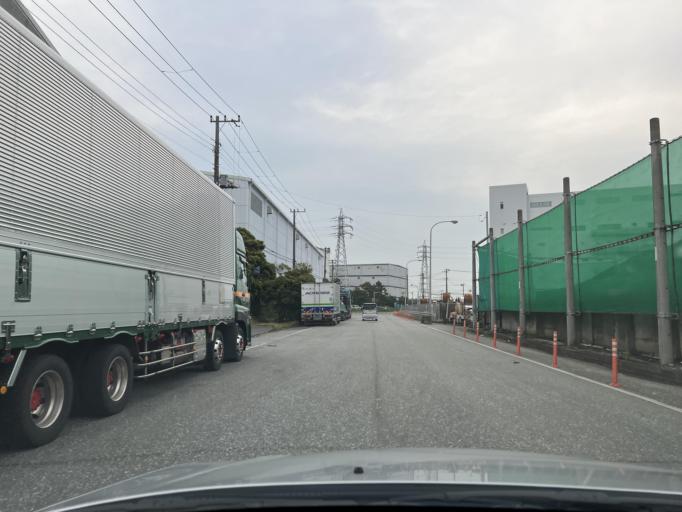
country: JP
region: Chiba
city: Funabashi
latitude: 35.6765
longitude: 139.9707
